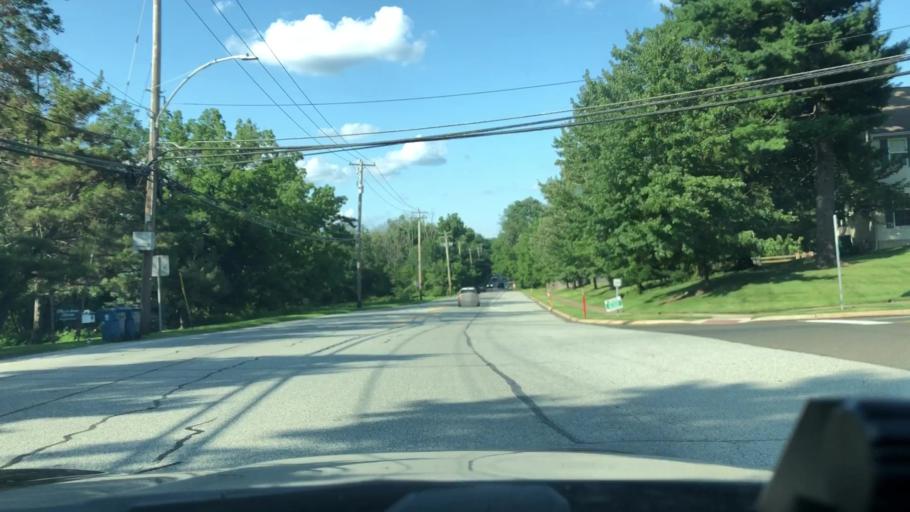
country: US
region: Pennsylvania
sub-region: Montgomery County
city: Montgomeryville
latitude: 40.2579
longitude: -75.2360
